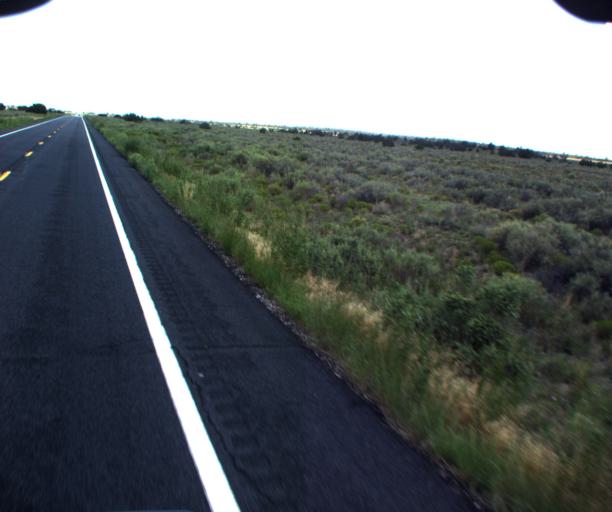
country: US
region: Arizona
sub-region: Coconino County
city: Grand Canyon Village
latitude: 35.6913
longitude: -112.1342
